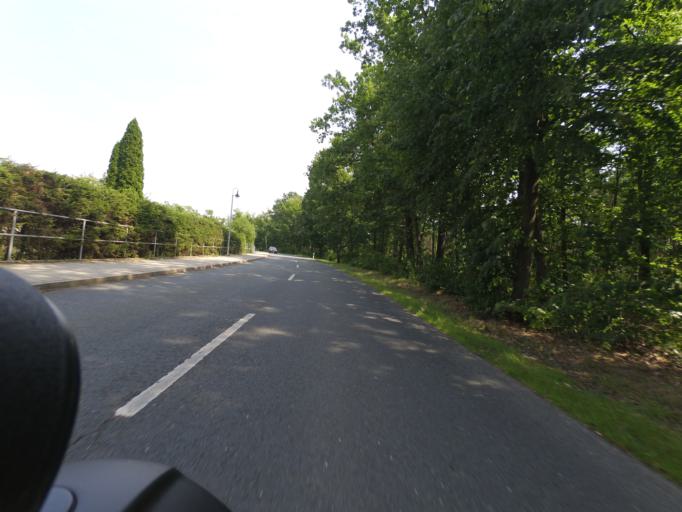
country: DE
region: Thuringia
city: Tautenhain
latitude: 50.9203
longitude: 11.9191
